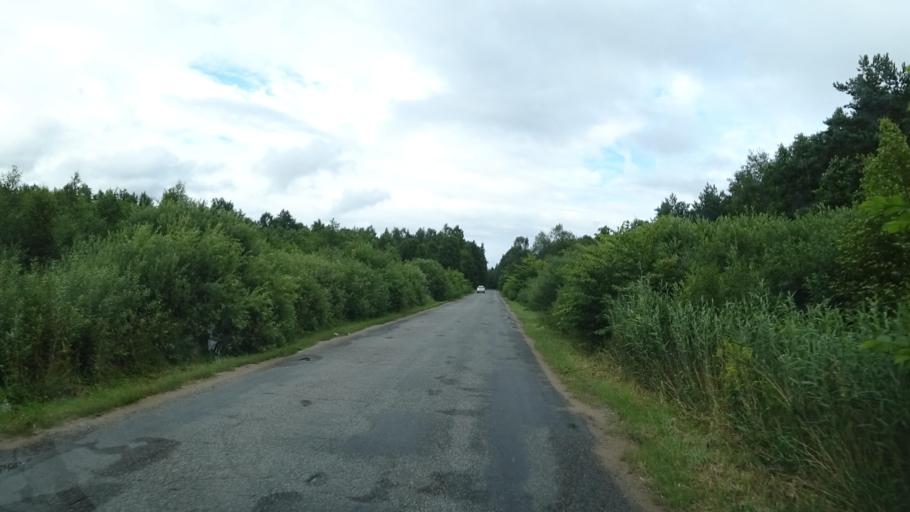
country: LV
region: Liepaja
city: Vec-Liepaja
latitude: 56.6006
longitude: 21.0317
